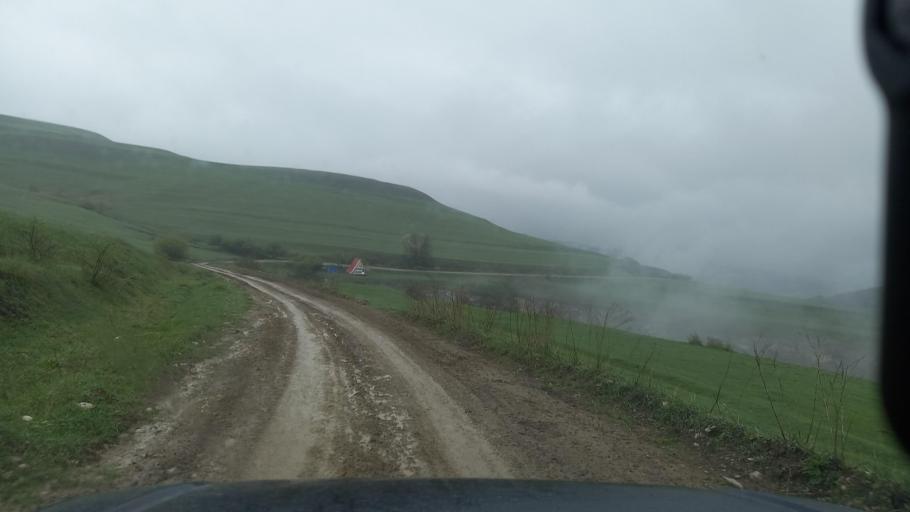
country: RU
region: Kabardino-Balkariya
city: Gundelen
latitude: 43.5930
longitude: 43.1219
